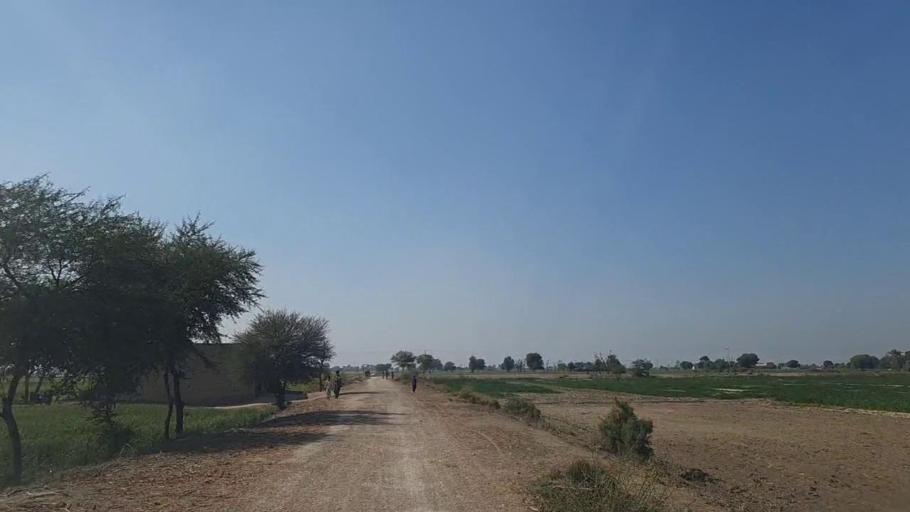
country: PK
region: Sindh
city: Shahpur Chakar
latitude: 26.2143
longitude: 68.5782
